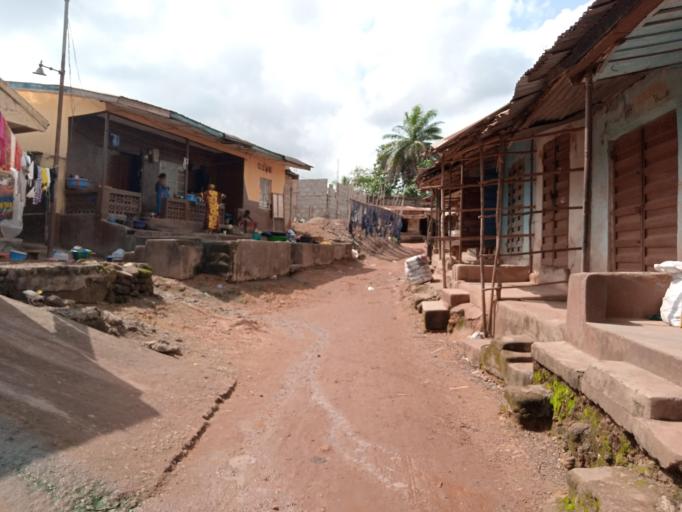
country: SL
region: Southern Province
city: Bo
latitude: 7.9635
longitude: -11.7360
